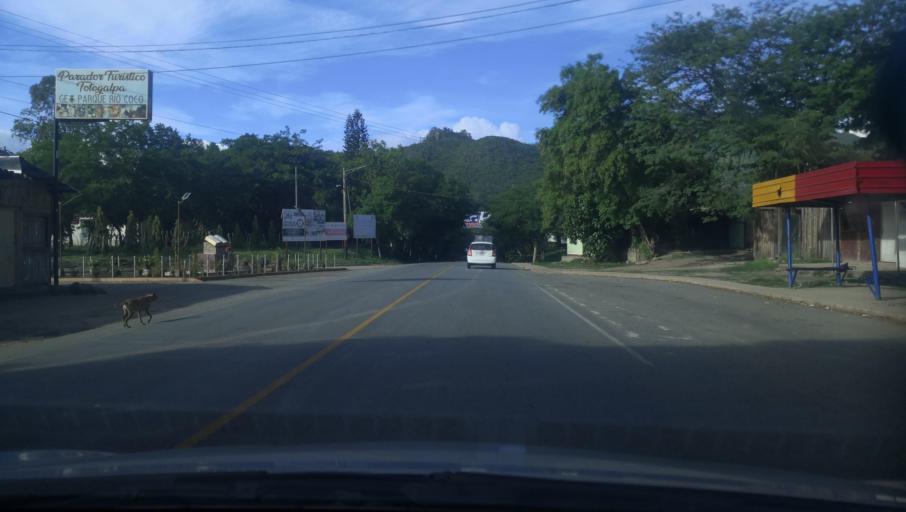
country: NI
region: Madriz
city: Totogalpa
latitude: 13.5624
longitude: -86.4890
